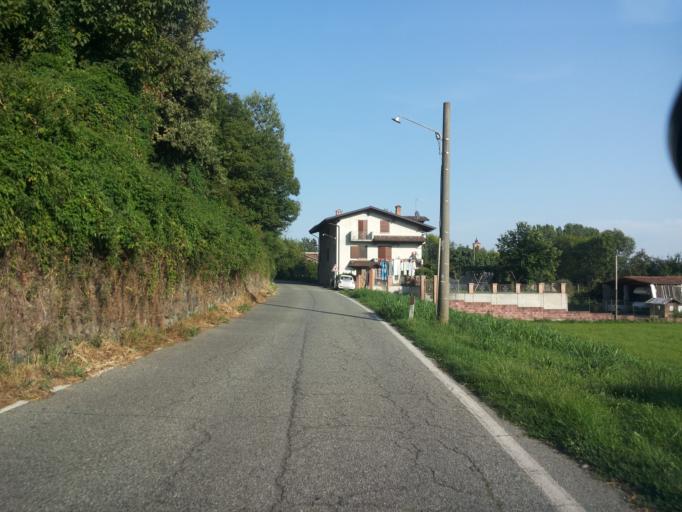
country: IT
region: Piedmont
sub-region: Provincia di Torino
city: Palazzo Canavese
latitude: 45.4610
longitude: 7.9730
